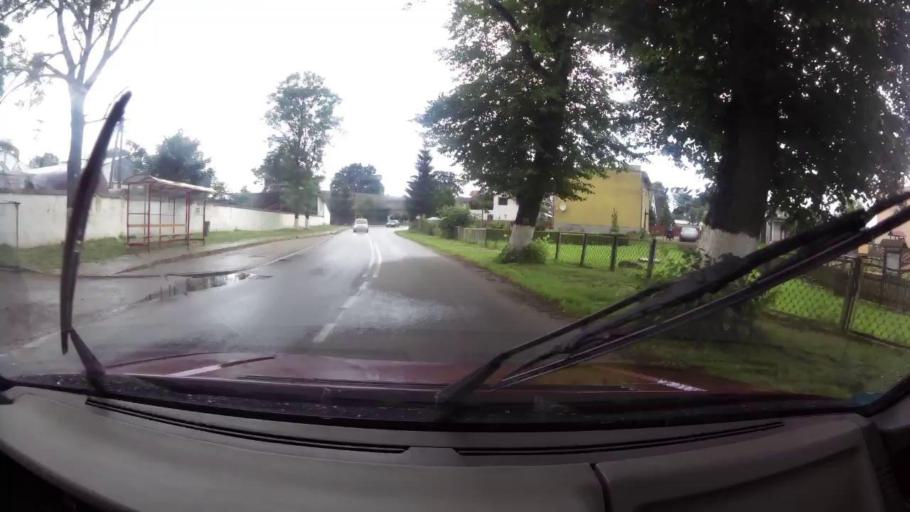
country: PL
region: West Pomeranian Voivodeship
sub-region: Koszalin
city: Koszalin
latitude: 54.1350
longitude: 16.1170
